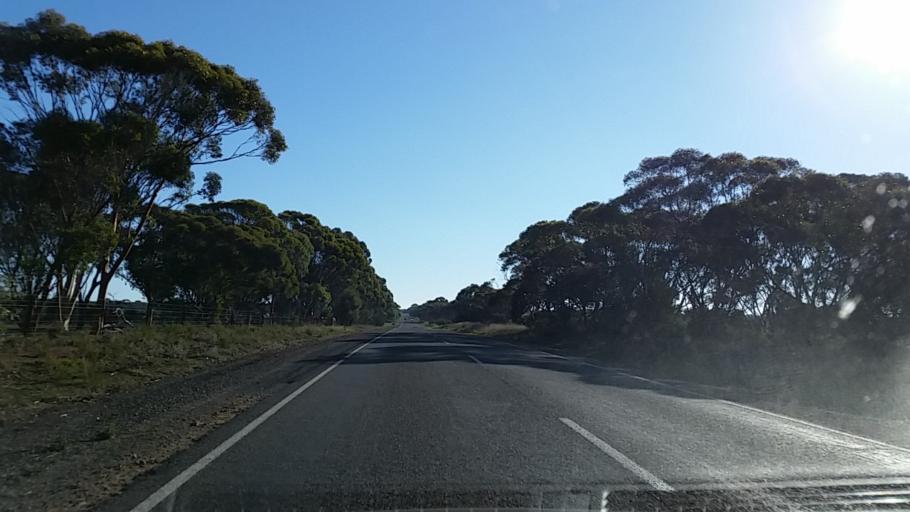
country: AU
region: South Australia
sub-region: Mount Barker
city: Callington
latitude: -35.1145
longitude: 139.0989
